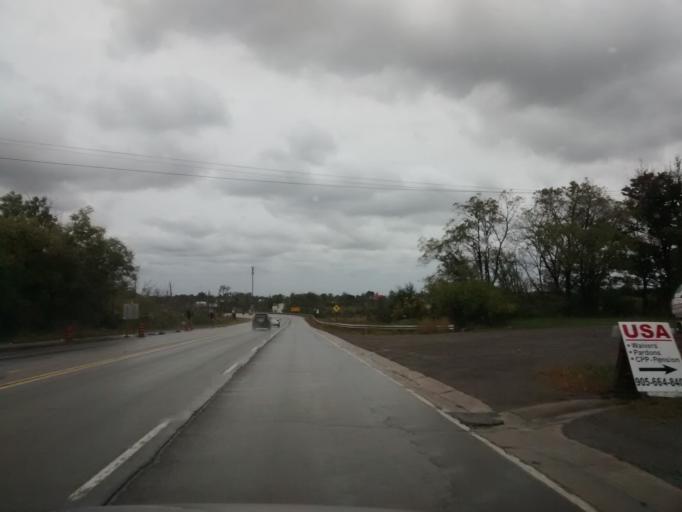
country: CA
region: Ontario
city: Hamilton
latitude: 43.1999
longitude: -79.7648
